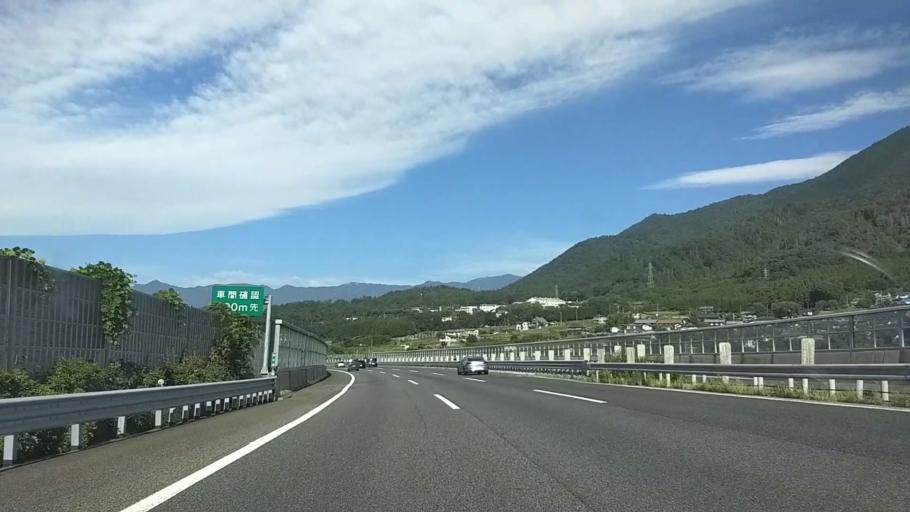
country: JP
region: Yamanashi
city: Otsuki
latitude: 35.6199
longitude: 138.9930
